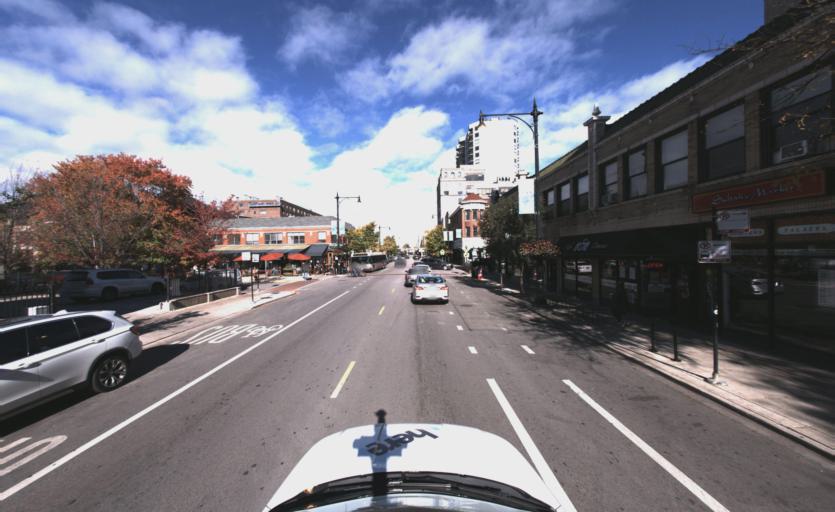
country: US
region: Illinois
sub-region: Cook County
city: Chicago
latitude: 41.9283
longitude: -87.6421
